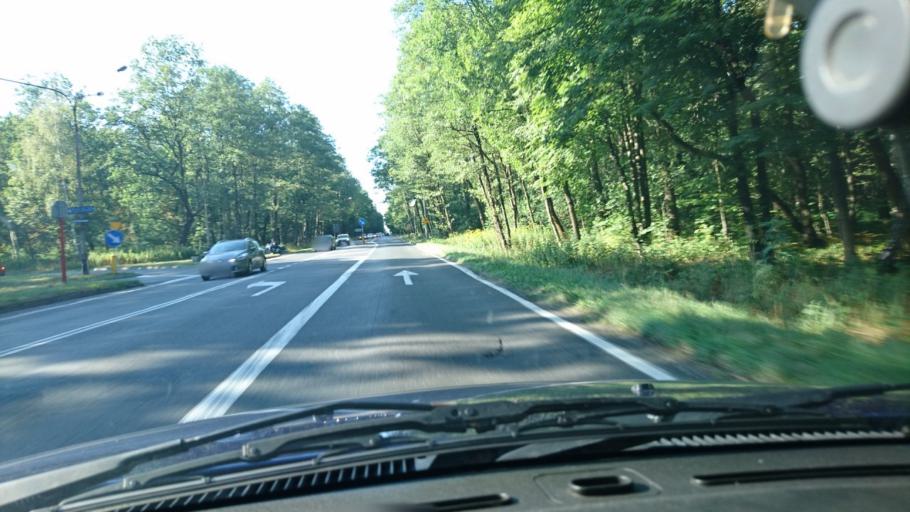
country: PL
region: Silesian Voivodeship
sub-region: Gliwice
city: Gliwice
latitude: 50.3384
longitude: 18.6538
